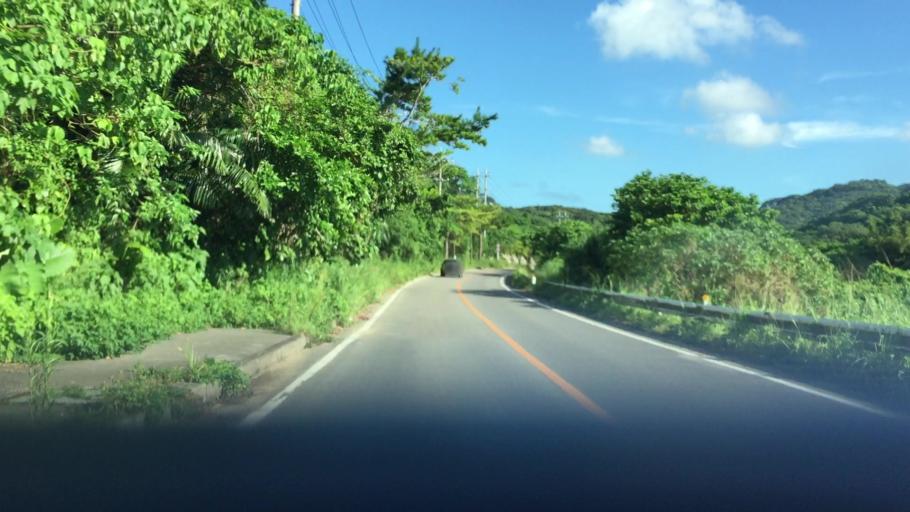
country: JP
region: Okinawa
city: Ishigaki
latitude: 24.3837
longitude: 124.1528
